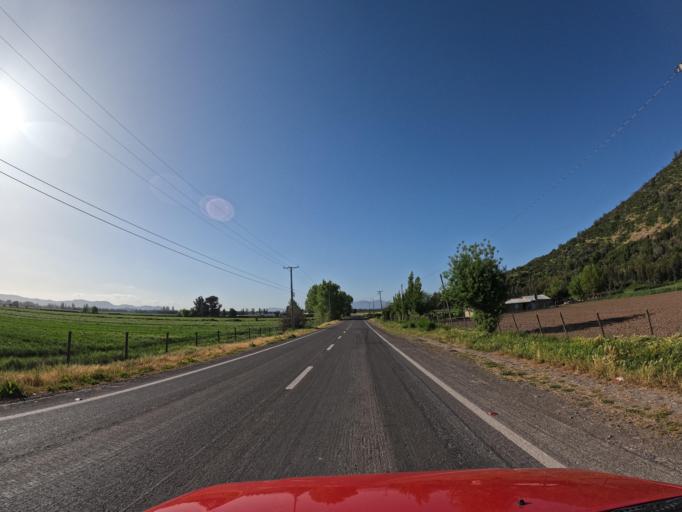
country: CL
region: Maule
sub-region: Provincia de Curico
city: Teno
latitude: -34.7774
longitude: -71.2309
